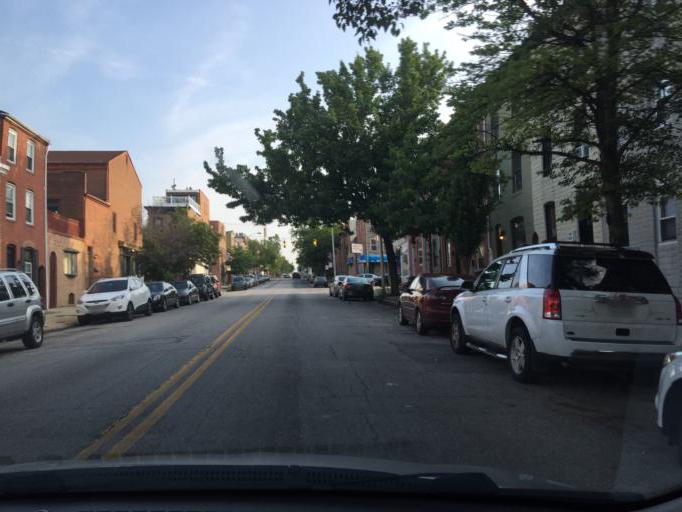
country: US
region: Maryland
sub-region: City of Baltimore
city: Baltimore
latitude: 39.2844
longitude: -76.5842
